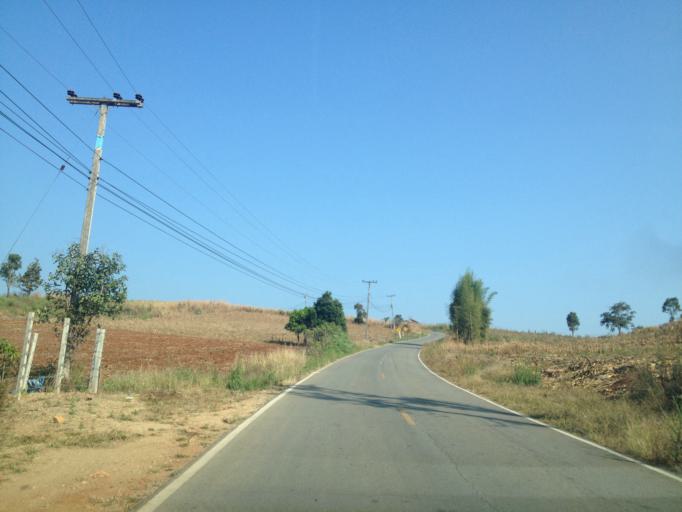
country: TH
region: Mae Hong Son
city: Ban Huai I Huak
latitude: 18.1100
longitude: 98.2191
